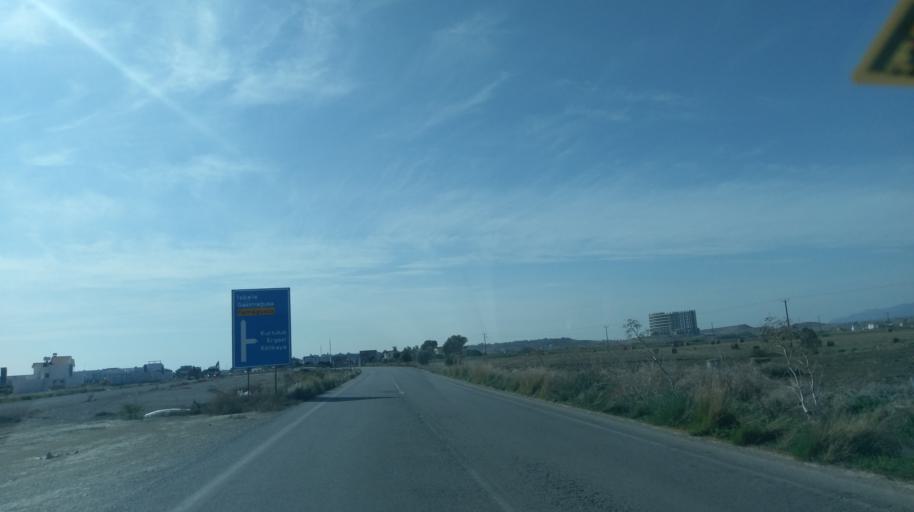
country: CY
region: Ammochostos
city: Trikomo
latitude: 35.3305
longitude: 33.9734
